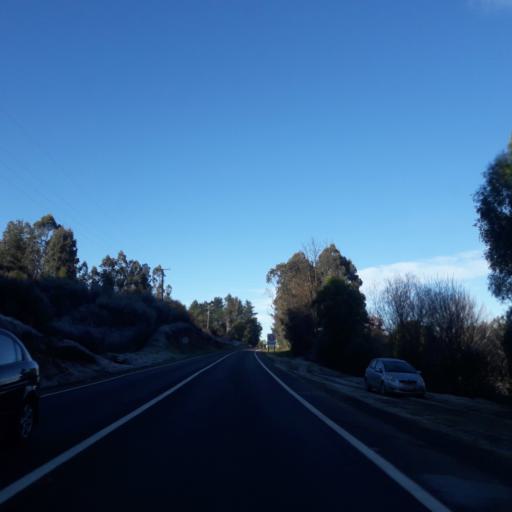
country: CL
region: Biobio
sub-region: Provincia de Biobio
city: La Laja
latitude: -37.3131
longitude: -72.9232
